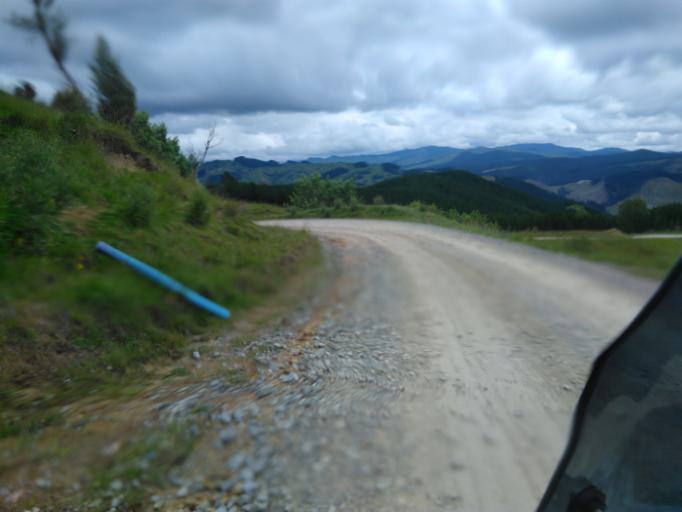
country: NZ
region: Gisborne
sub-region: Gisborne District
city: Gisborne
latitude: -38.0902
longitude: 178.0823
